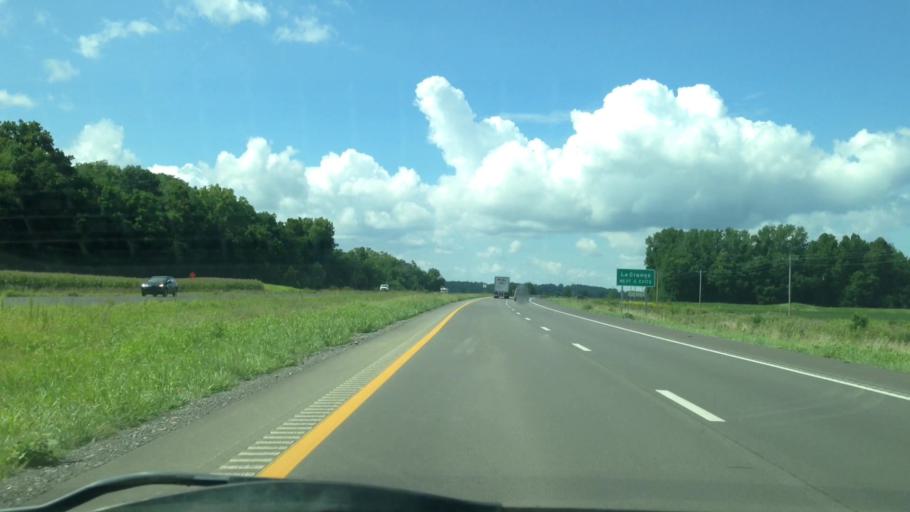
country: US
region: Illinois
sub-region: Adams County
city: Quincy
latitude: 39.9792
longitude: -91.5241
